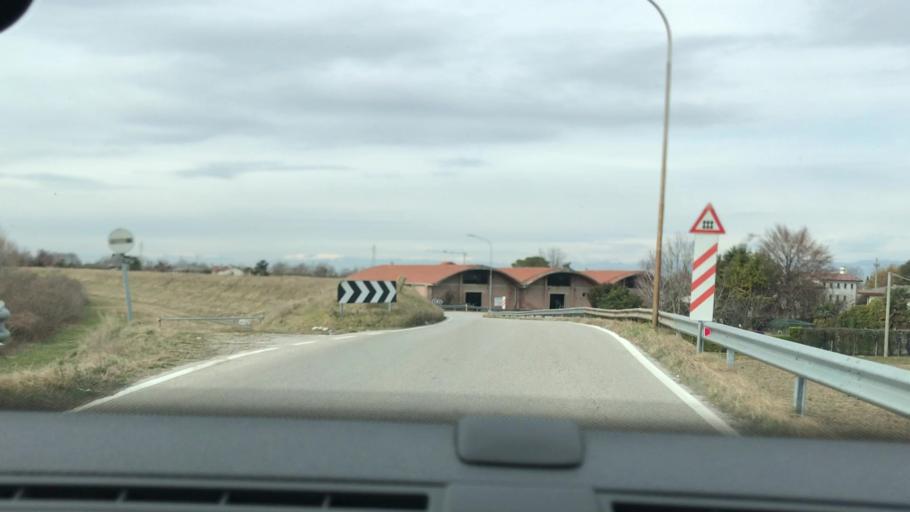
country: IT
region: Veneto
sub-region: Provincia di Venezia
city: Santo Stino di Livenza
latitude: 45.7183
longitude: 12.6828
